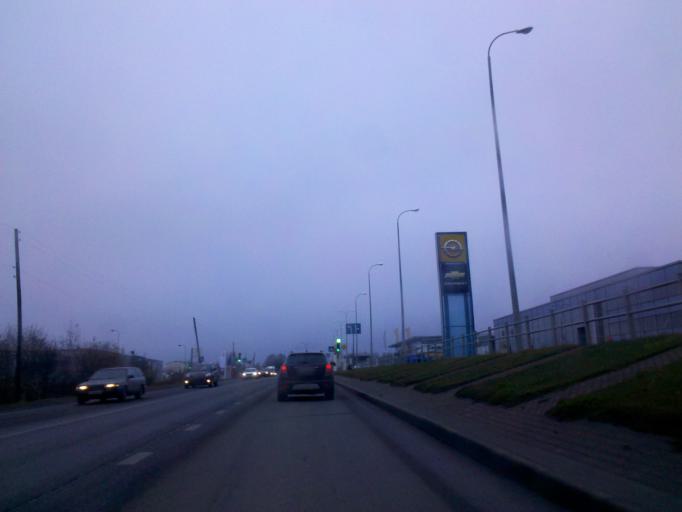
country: RU
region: Republic of Karelia
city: Petrozavodsk
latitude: 61.8197
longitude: 34.2763
